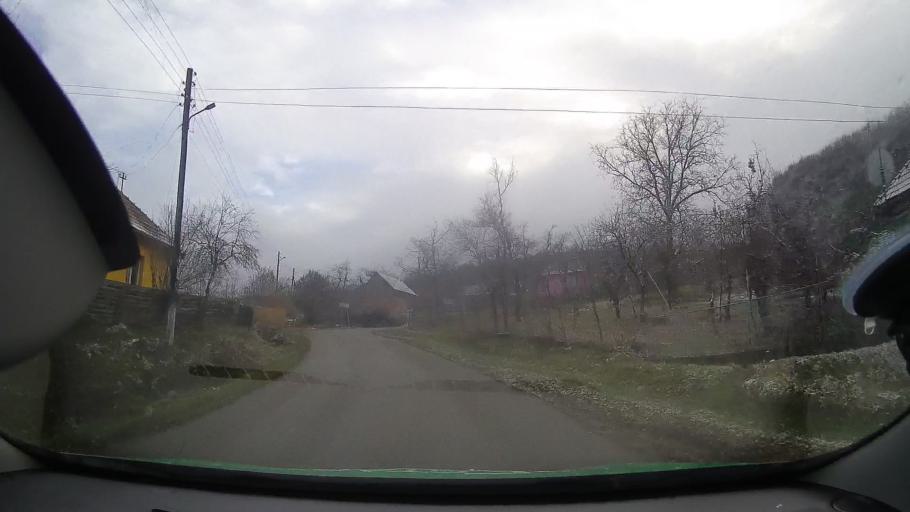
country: RO
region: Mures
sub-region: Comuna Chetani
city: Chetani
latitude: 46.4040
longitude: 24.0132
